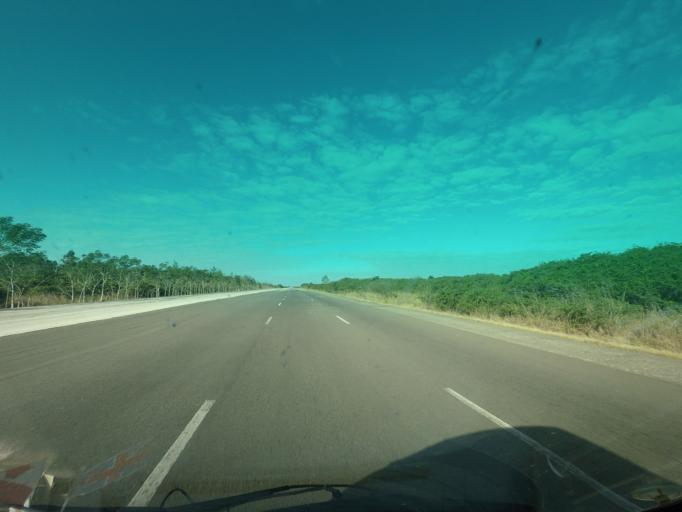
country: CU
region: Cienfuegos
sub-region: Municipio de Aguada de Pasajeros
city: Aguada de Pasajeros
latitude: 22.4364
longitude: -80.6981
